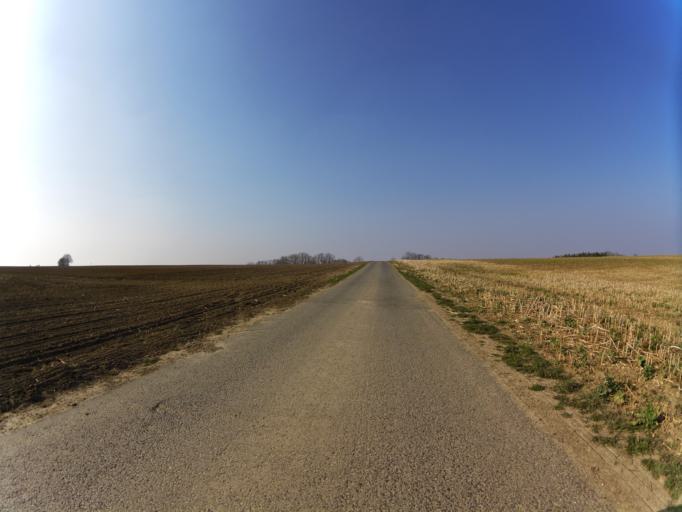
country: DE
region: Bavaria
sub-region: Regierungsbezirk Unterfranken
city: Gaukonigshofen
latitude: 49.6613
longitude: 9.9929
